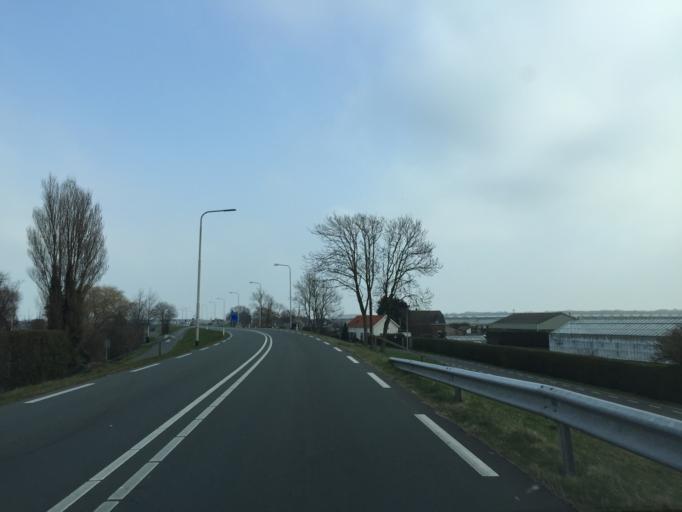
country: NL
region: South Holland
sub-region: Gemeente Westland
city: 's-Gravenzande
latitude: 51.9891
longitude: 4.1568
